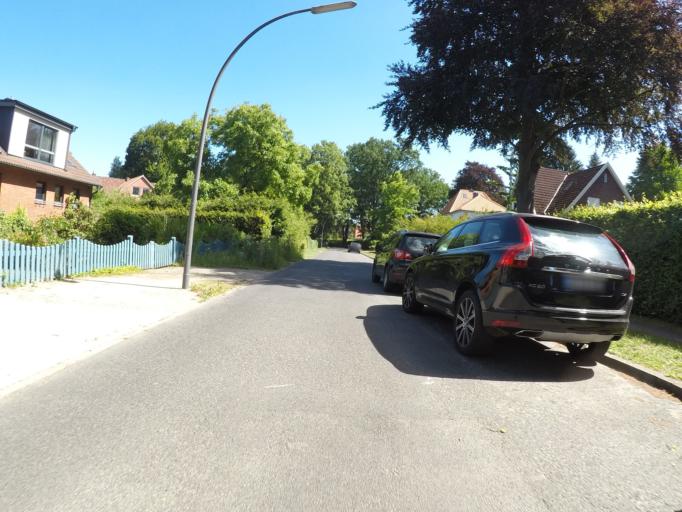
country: DE
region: Hamburg
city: Bergstedt
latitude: 53.6400
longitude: 10.1479
